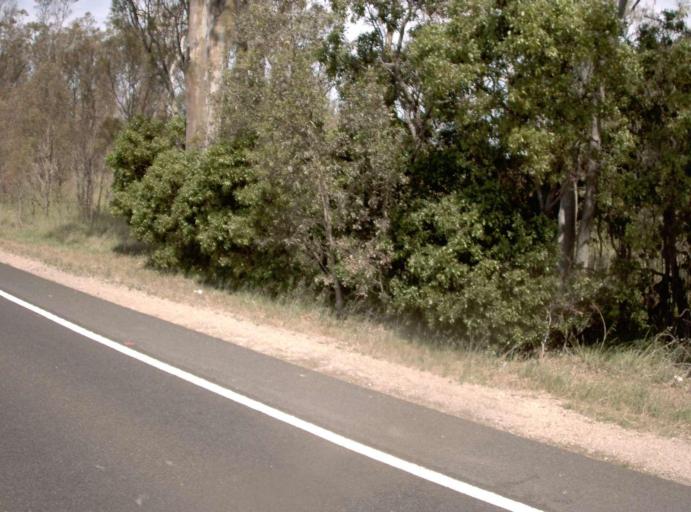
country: AU
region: Victoria
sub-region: East Gippsland
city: Bairnsdale
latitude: -37.8739
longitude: 147.4545
